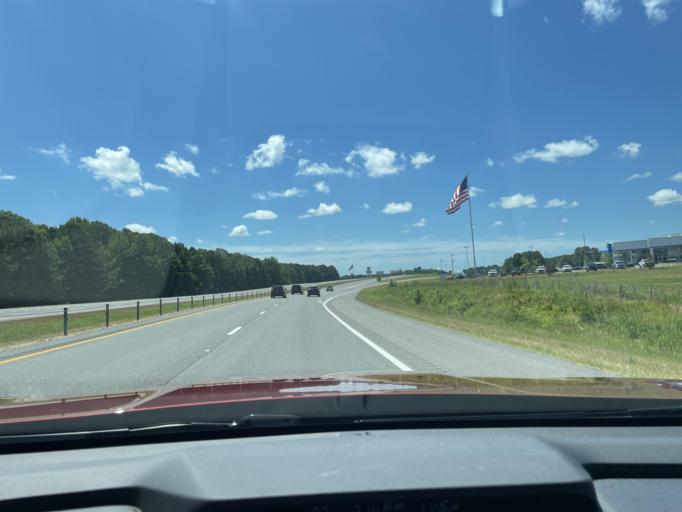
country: US
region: Arkansas
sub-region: Jefferson County
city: White Hall
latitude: 34.2669
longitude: -92.1061
